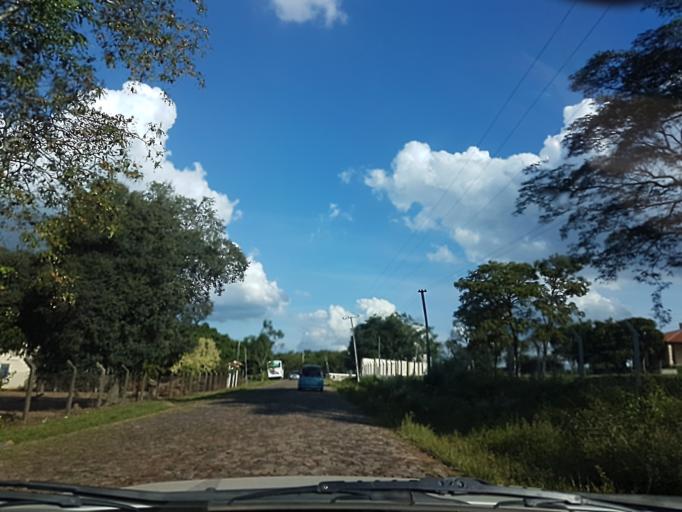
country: PY
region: Cordillera
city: Arroyos y Esteros
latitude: -25.0028
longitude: -57.1361
